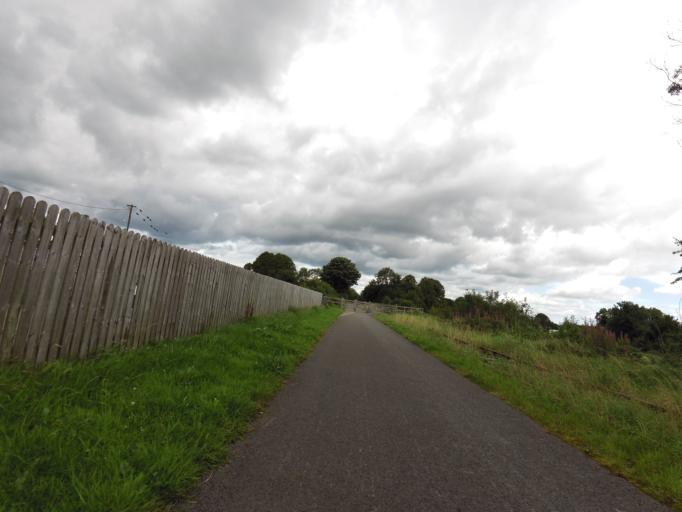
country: IE
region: Leinster
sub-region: An Iarmhi
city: An Muileann gCearr
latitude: 53.5025
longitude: -7.4316
